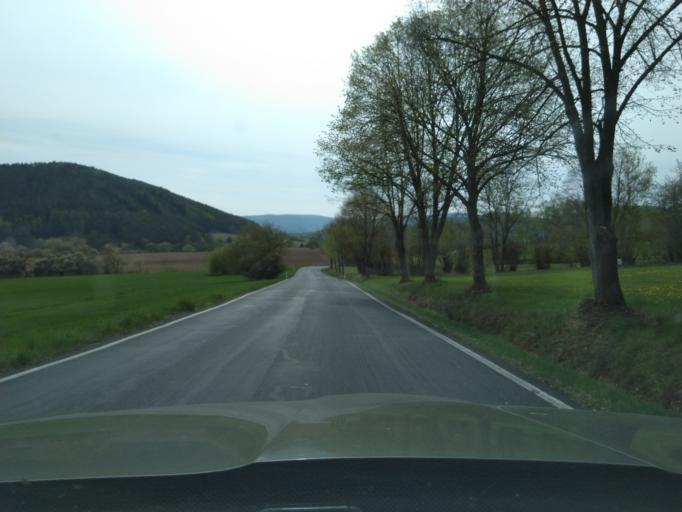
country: CZ
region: Plzensky
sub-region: Okres Klatovy
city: Susice
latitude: 49.2405
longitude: 13.5768
